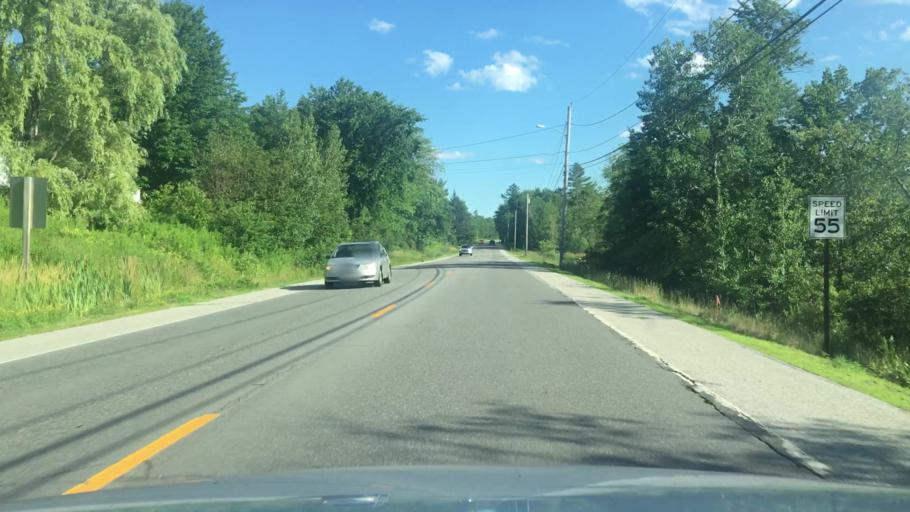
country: US
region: Maine
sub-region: Franklin County
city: Jay
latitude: 44.5449
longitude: -70.2372
